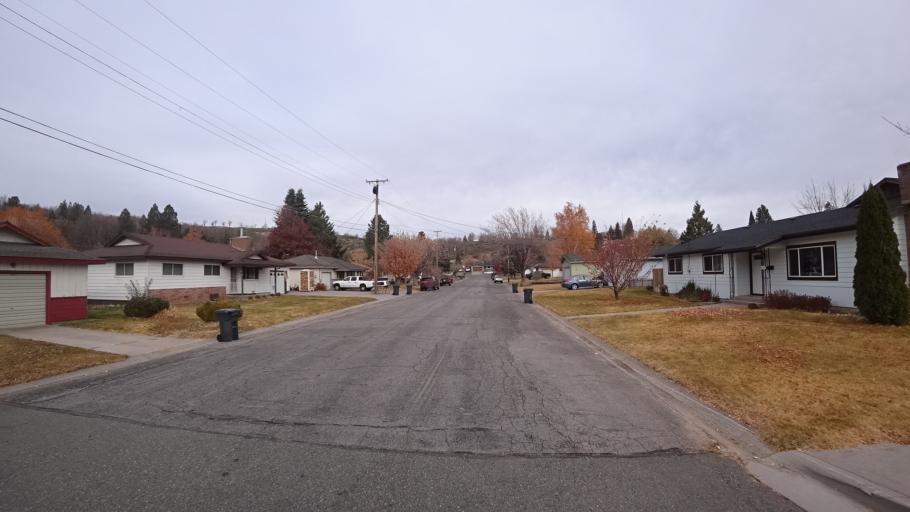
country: US
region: California
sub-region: Siskiyou County
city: Weed
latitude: 41.4159
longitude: -122.3893
